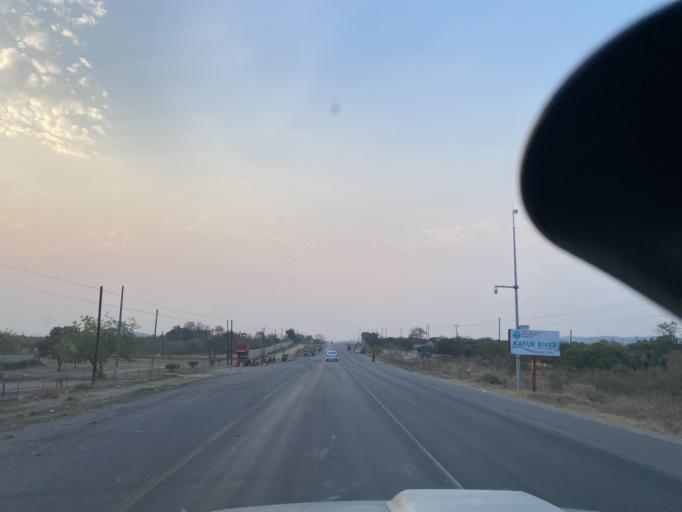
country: ZM
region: Lusaka
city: Kafue
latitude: -15.8367
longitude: 28.2366
